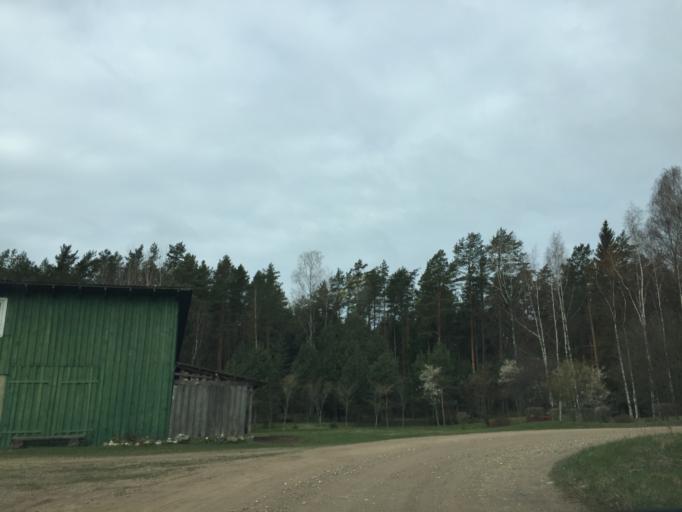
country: LV
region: Saulkrastu
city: Saulkrasti
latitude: 57.5018
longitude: 24.4269
